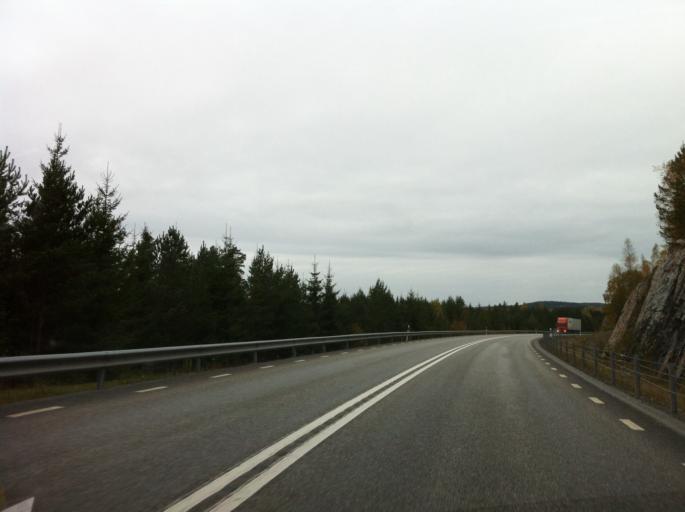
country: SE
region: OErebro
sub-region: Ljusnarsbergs Kommun
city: Kopparberg
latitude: 59.8523
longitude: 15.0618
